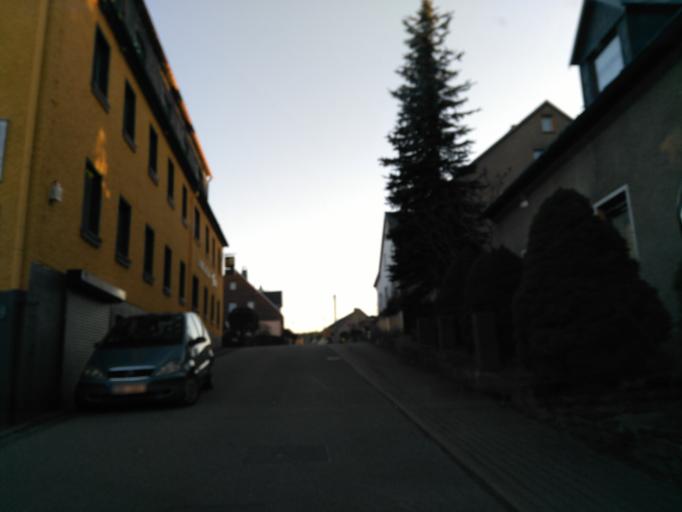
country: CZ
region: Ustecky
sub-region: Okres Chomutov
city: Vejprty
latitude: 50.4912
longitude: 13.0211
